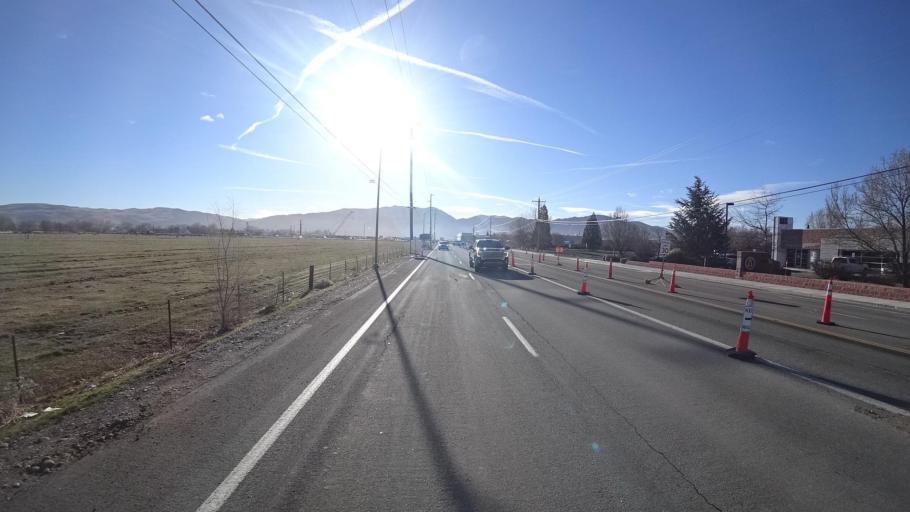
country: US
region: Nevada
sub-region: Washoe County
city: Sparks
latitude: 39.5132
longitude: -119.7485
